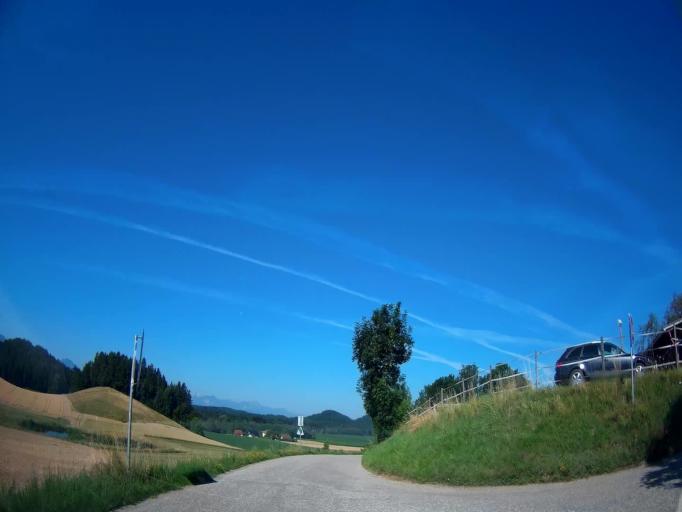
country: AT
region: Carinthia
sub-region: Politischer Bezirk Klagenfurt Land
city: Poggersdorf
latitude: 46.6776
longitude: 14.5139
